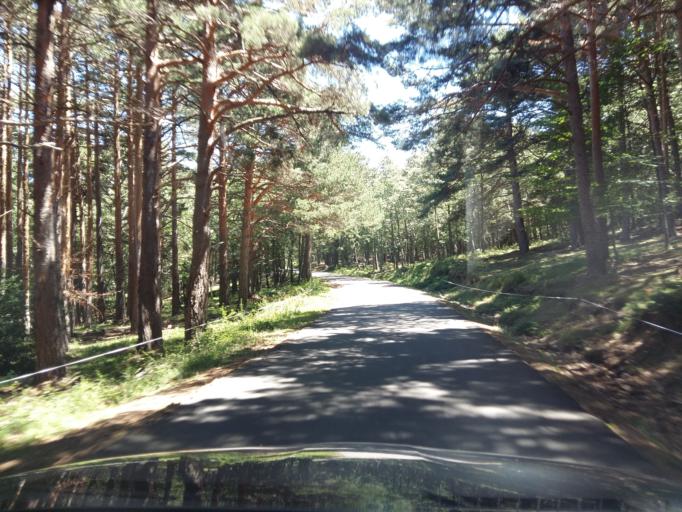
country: ES
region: Castille and Leon
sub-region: Provincia de Soria
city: Vozmediano
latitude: 41.8101
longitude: -1.8112
